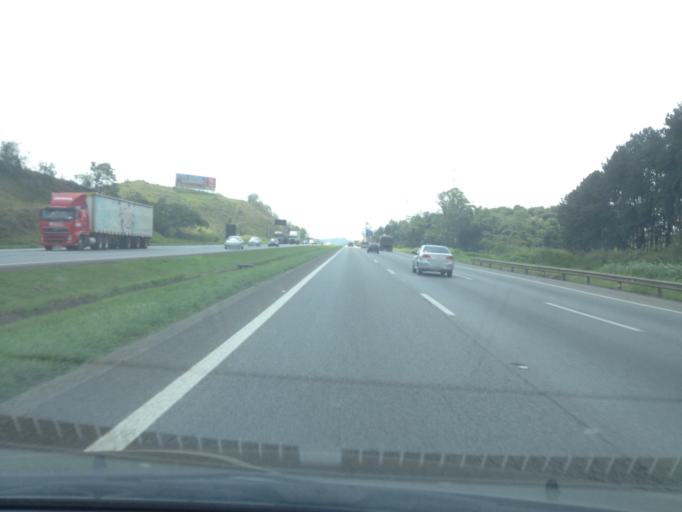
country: BR
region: Sao Paulo
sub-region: Itapevi
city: Itapevi
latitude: -23.4904
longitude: -46.9883
